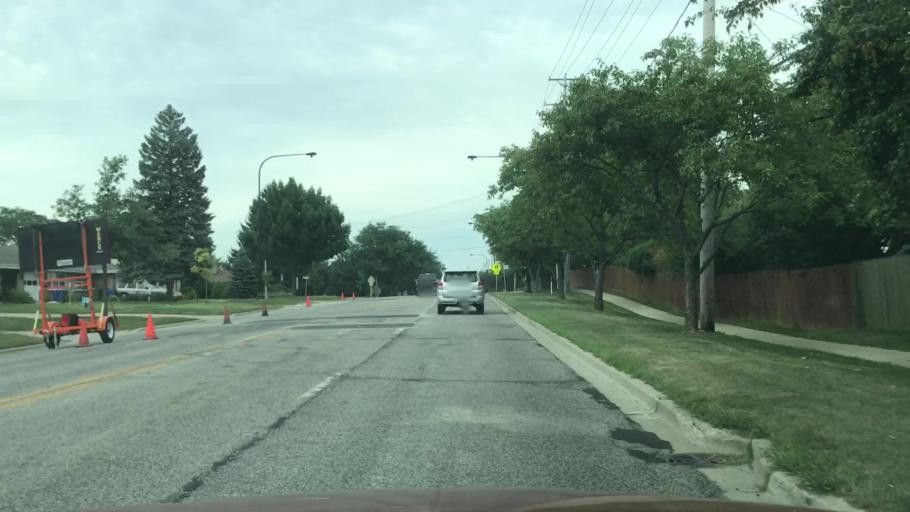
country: US
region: Illinois
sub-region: Cook County
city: Mount Prospect
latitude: 42.0663
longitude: -87.9534
